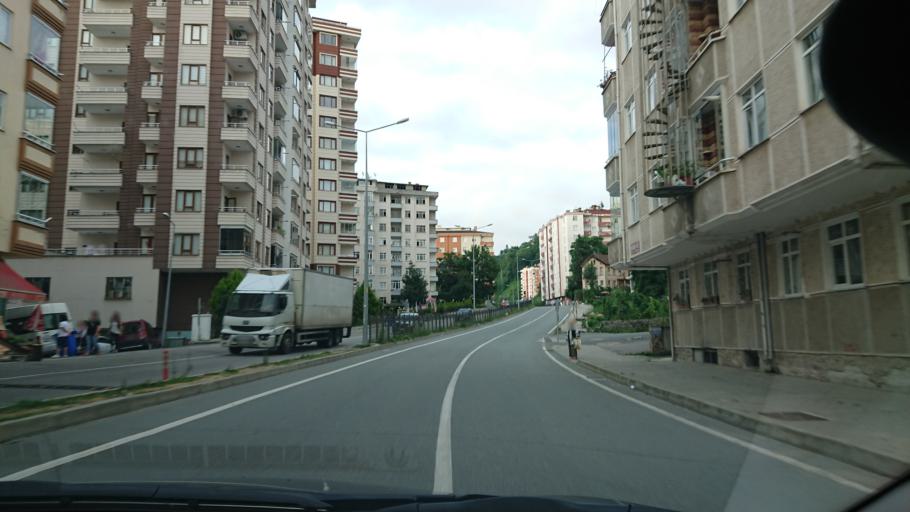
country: TR
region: Rize
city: Rize
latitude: 41.0249
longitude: 40.5452
